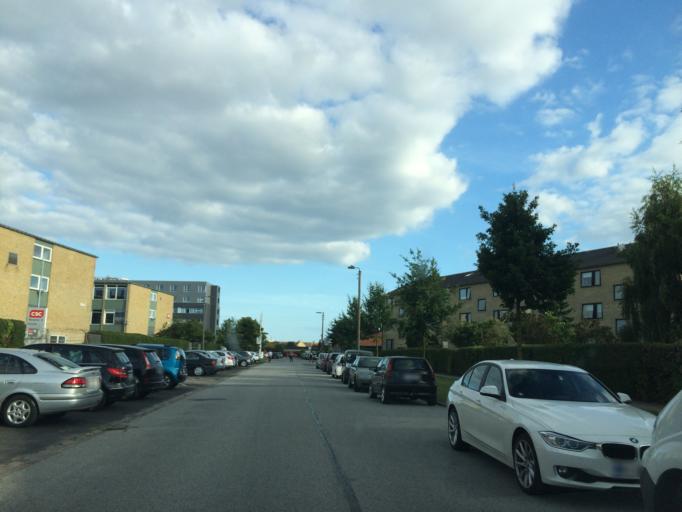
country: DK
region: Capital Region
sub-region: Tarnby Kommune
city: Tarnby
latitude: 55.6463
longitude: 12.6355
